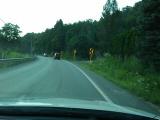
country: US
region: Pennsylvania
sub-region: Potter County
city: Coudersport
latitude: 41.7656
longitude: -78.1188
